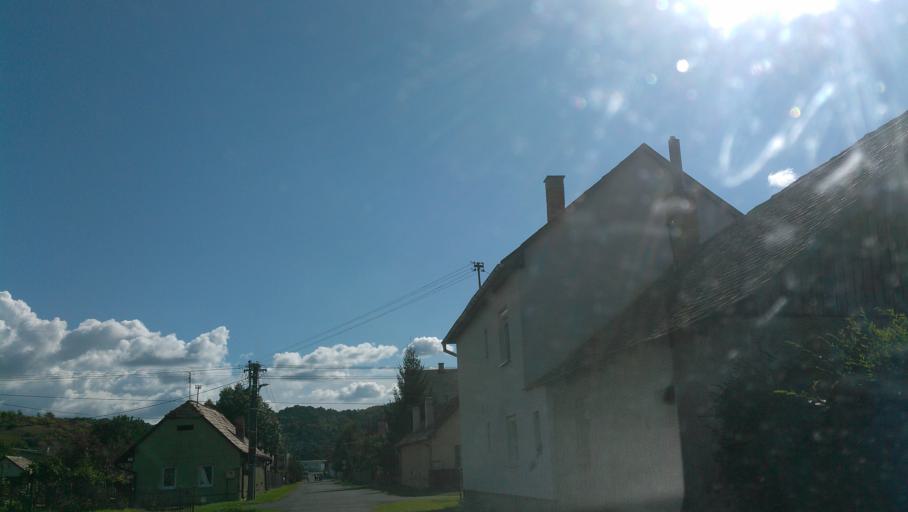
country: SK
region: Banskobystricky
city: Poltar
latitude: 48.3797
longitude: 19.8901
